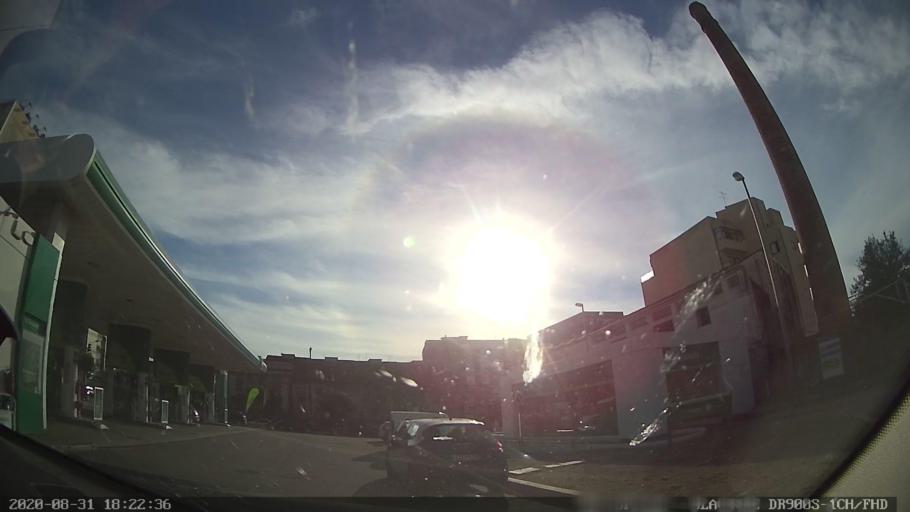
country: PT
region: Porto
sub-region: Porto
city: Porto
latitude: 41.1633
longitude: -8.6329
